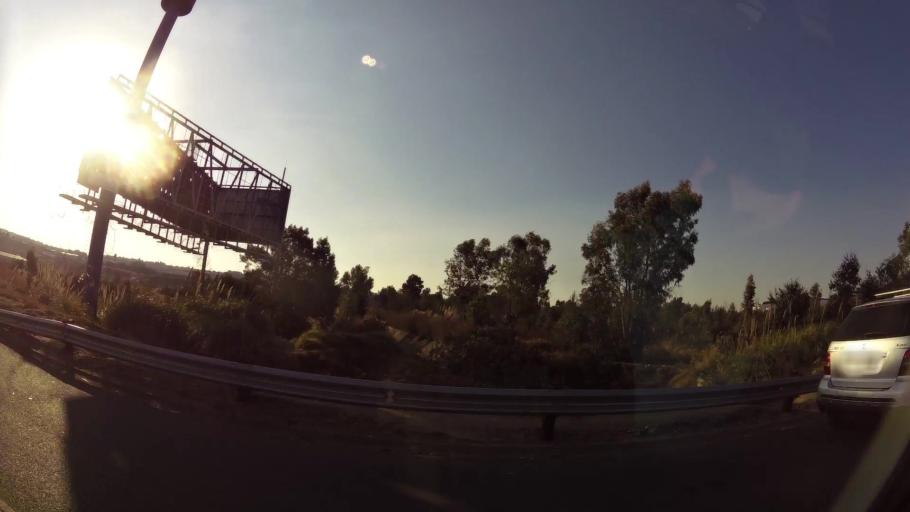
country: ZA
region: Gauteng
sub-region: Ekurhuleni Metropolitan Municipality
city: Germiston
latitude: -26.2103
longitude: 28.1124
